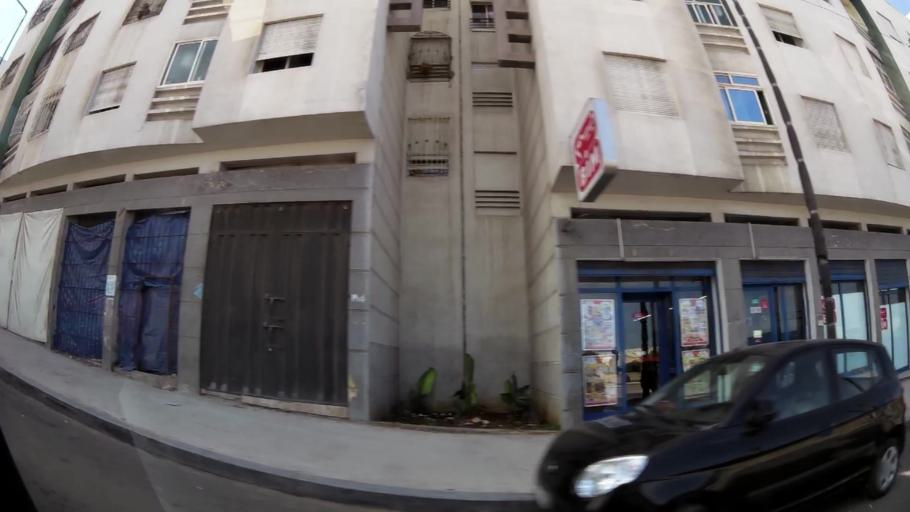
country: MA
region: Grand Casablanca
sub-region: Mediouna
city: Tit Mellil
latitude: 33.6086
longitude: -7.5204
